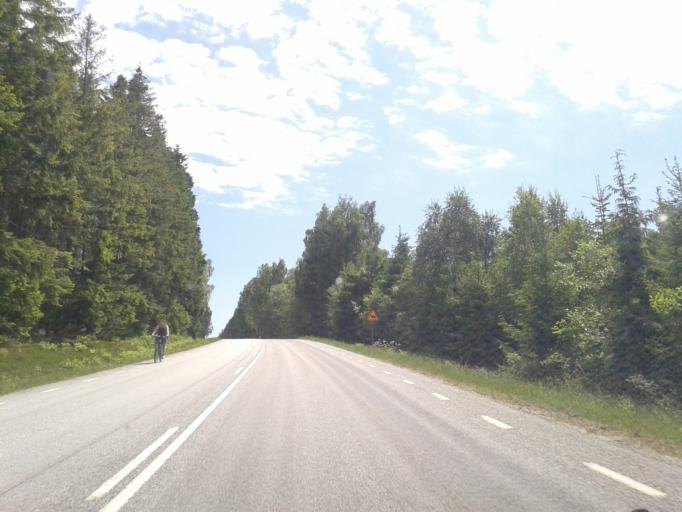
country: SE
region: Vaestra Goetaland
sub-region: Uddevalla Kommun
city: Ljungskile
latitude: 58.1713
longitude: 11.9638
